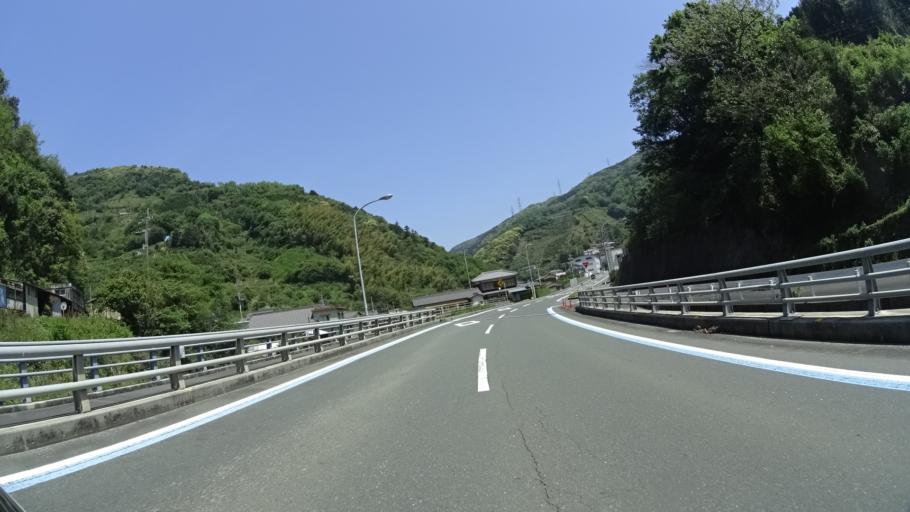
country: JP
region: Ehime
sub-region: Nishiuwa-gun
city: Ikata-cho
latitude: 33.5024
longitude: 132.3963
